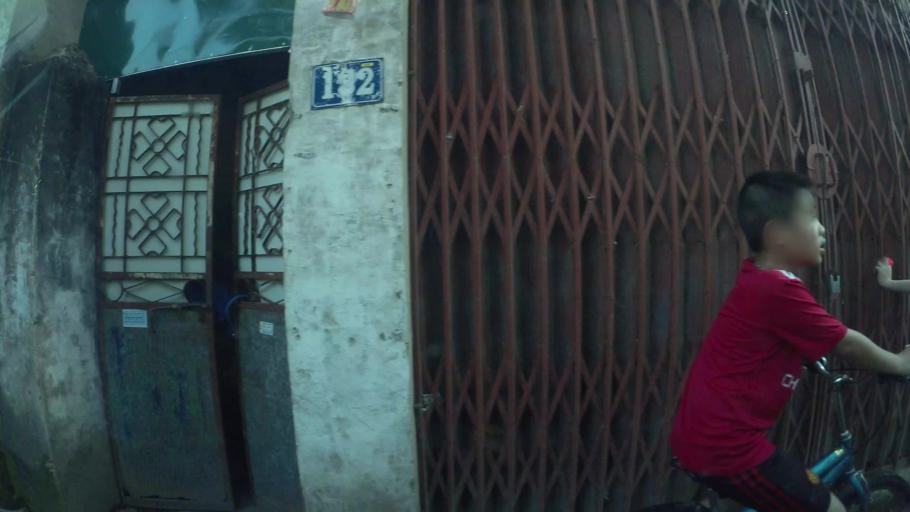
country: VN
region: Ha Noi
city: Thanh Xuan
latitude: 20.9792
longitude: 105.8288
